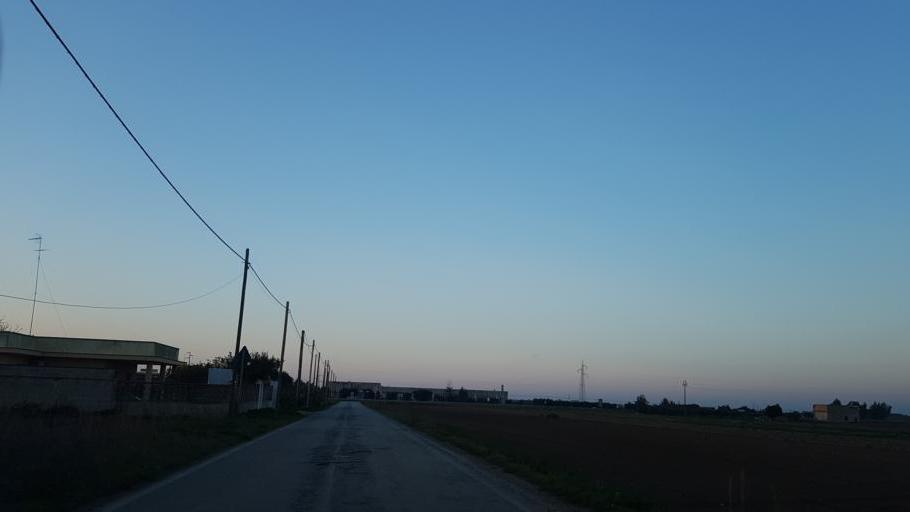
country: IT
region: Apulia
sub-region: Provincia di Brindisi
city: Brindisi
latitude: 40.6056
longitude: 17.8907
